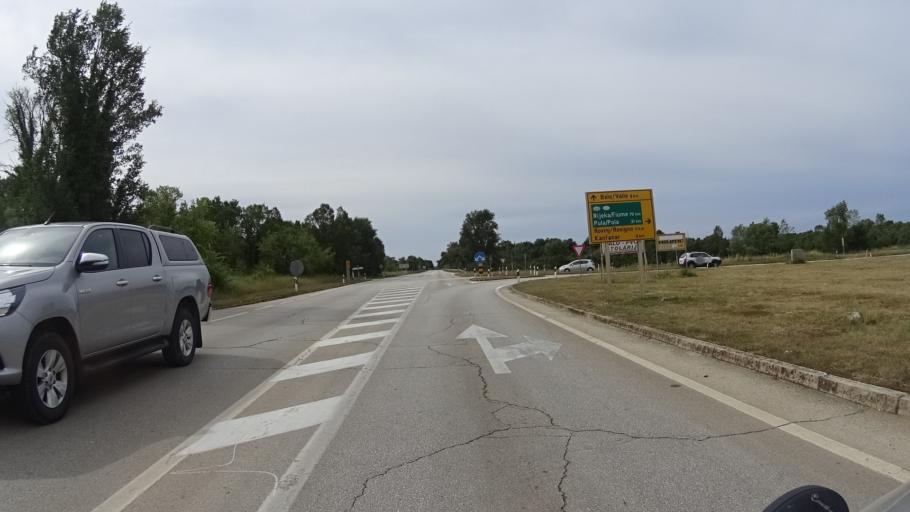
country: HR
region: Istarska
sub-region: Grad Rovinj
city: Rovinj
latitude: 45.1100
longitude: 13.7678
